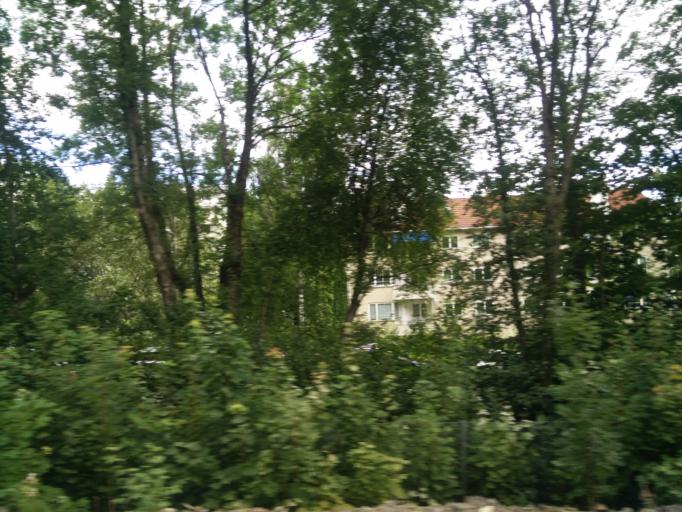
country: NO
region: Oslo
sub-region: Oslo
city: Sjolyststranda
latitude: 59.9468
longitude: 10.6632
